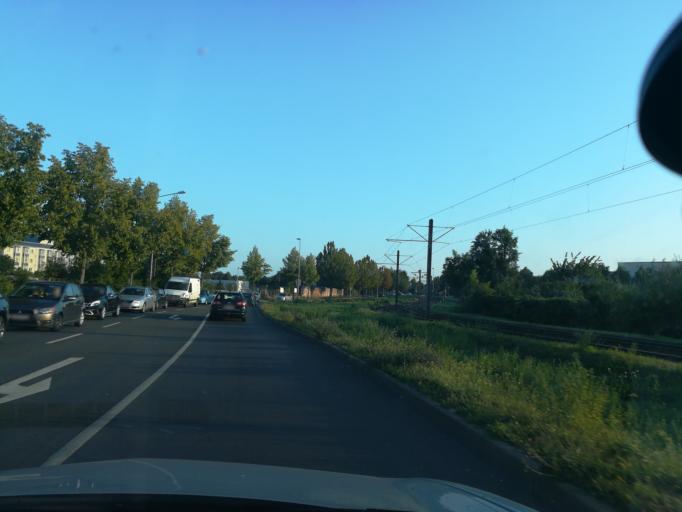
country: DE
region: Saxony-Anhalt
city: Magdeburg
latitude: 52.1359
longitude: 11.6035
